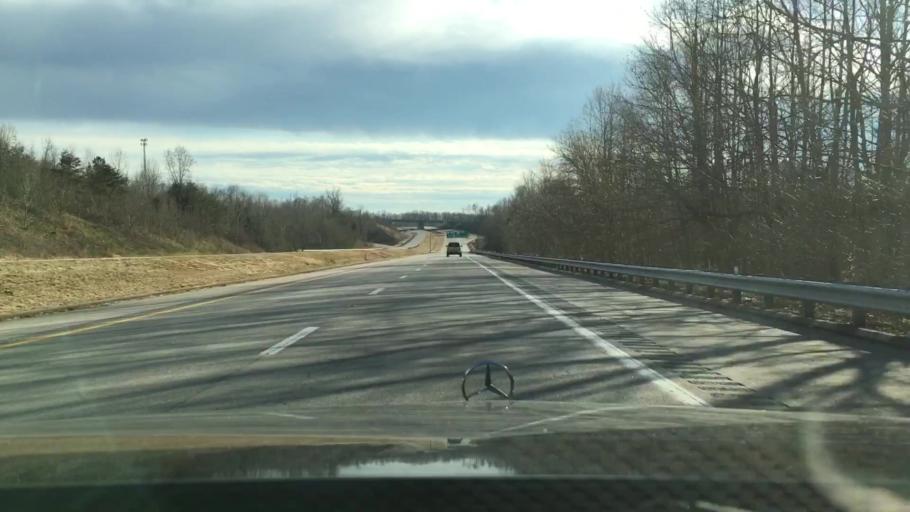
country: US
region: Virginia
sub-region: City of Danville
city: Danville
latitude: 36.6245
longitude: -79.3651
